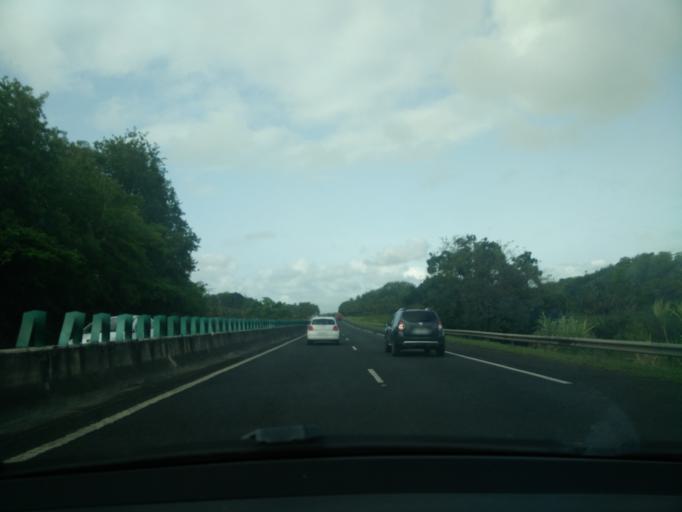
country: GP
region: Guadeloupe
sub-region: Guadeloupe
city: Les Abymes
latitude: 16.2888
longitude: -61.5043
